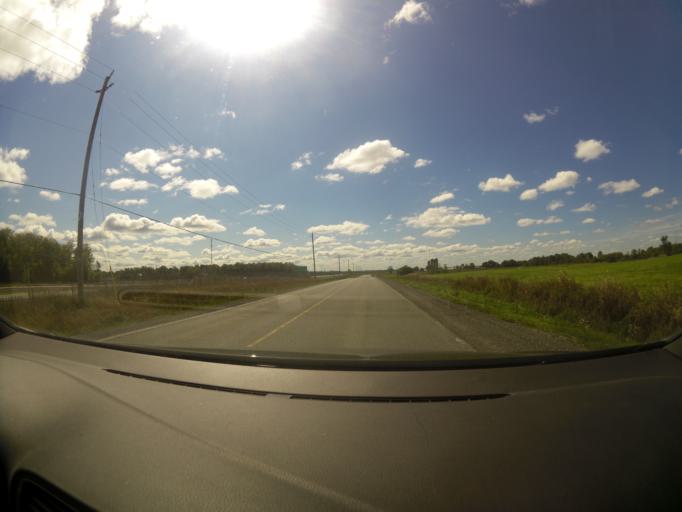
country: CA
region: Ontario
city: Carleton Place
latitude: 45.1604
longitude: -76.0756
